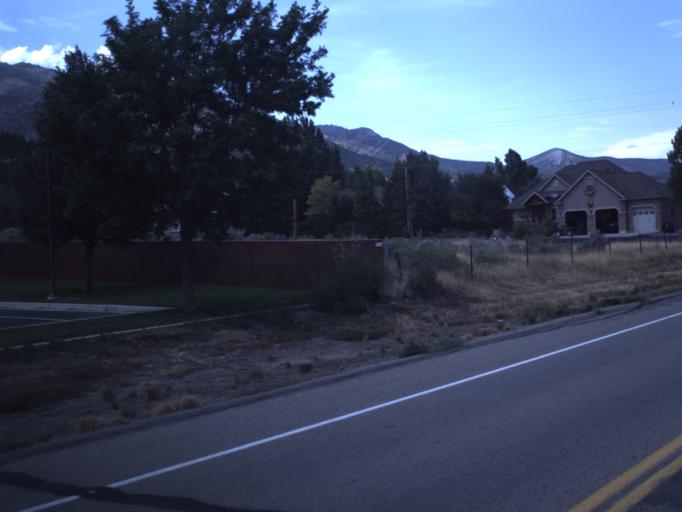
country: US
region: Utah
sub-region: Utah County
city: Eagle Mountain
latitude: 40.3282
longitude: -112.1023
